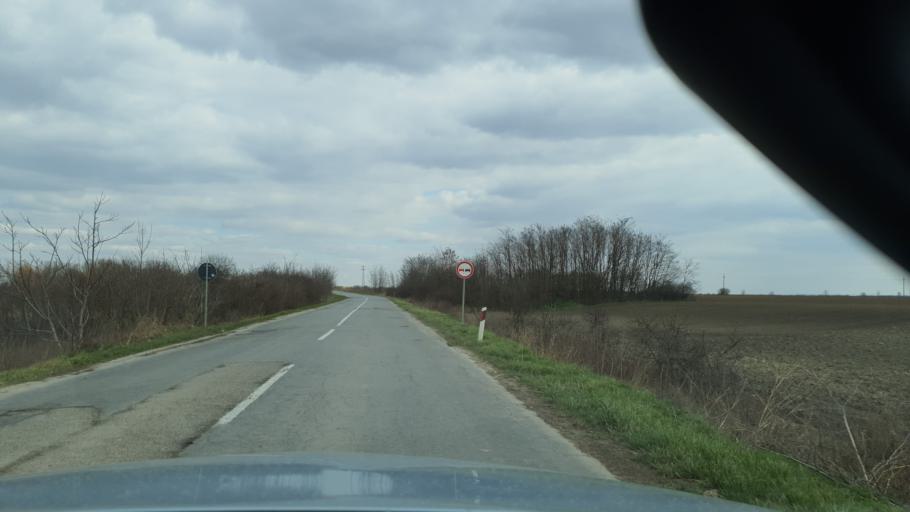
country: RS
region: Autonomna Pokrajina Vojvodina
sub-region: Juznobacki Okrug
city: Bac
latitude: 45.3969
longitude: 19.2578
